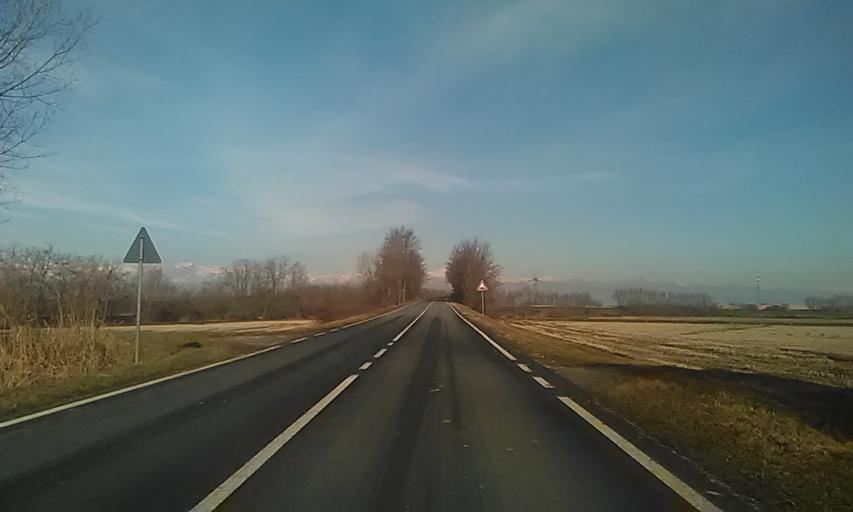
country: IT
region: Piedmont
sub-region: Provincia di Vercelli
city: Formigliana
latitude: 45.4383
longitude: 8.2936
